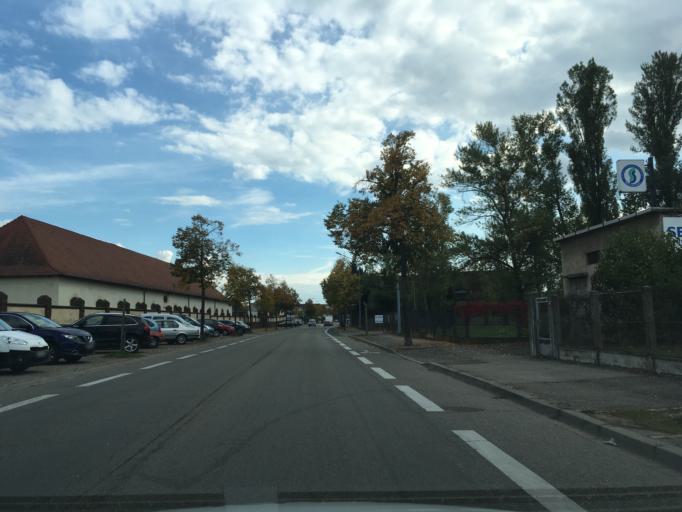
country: FR
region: Alsace
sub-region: Departement du Haut-Rhin
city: Colmar
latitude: 48.0922
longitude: 7.3562
